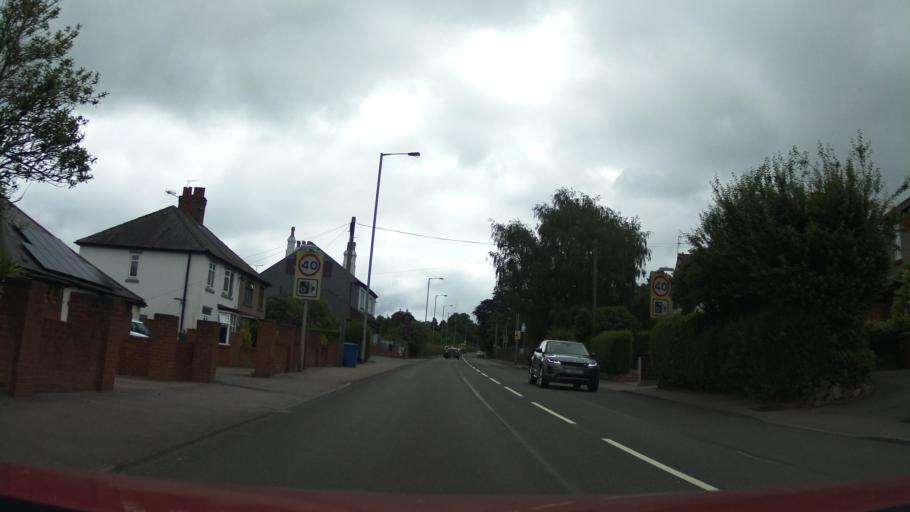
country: GB
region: England
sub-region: Staffordshire
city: Burton upon Trent
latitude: 52.8040
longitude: -1.6073
